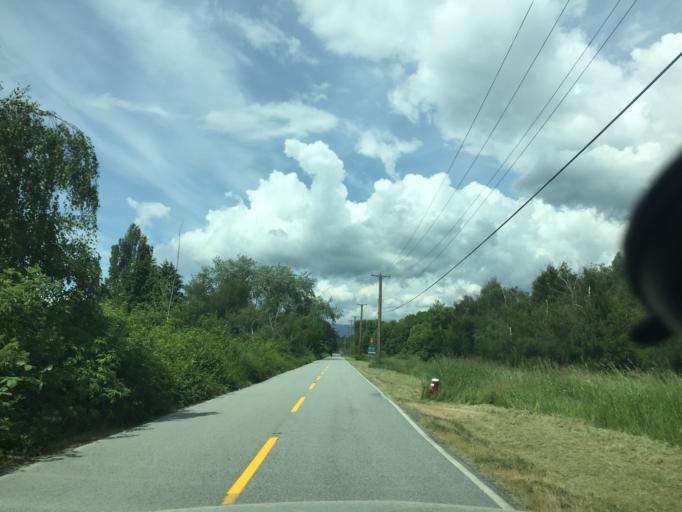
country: CA
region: British Columbia
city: Richmond
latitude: 49.2079
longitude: -123.1698
